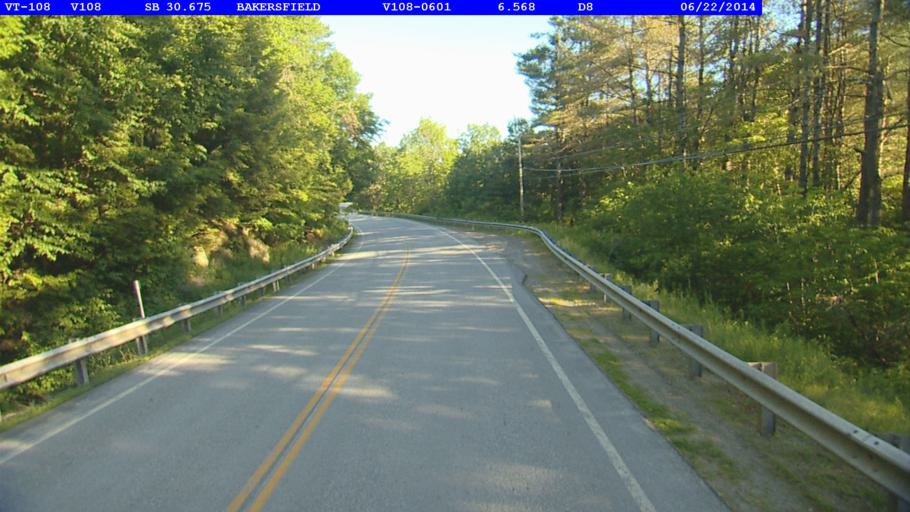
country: US
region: Vermont
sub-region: Franklin County
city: Enosburg Falls
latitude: 44.8207
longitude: -72.7924
